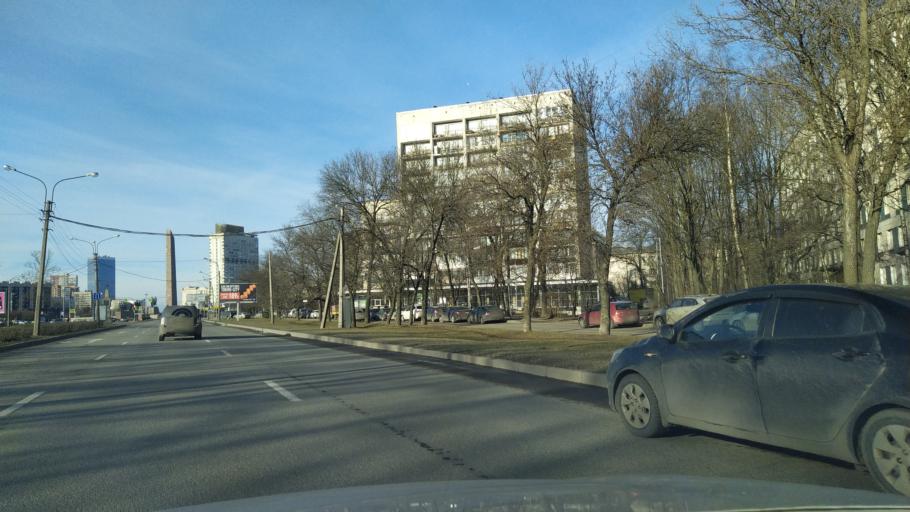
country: RU
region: St.-Petersburg
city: Kupchino
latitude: 59.8403
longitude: 30.3270
